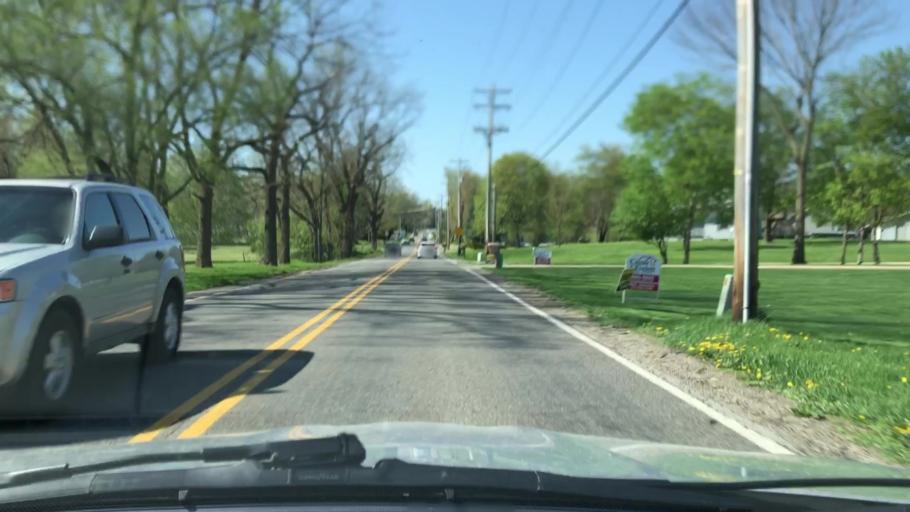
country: US
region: Indiana
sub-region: Saint Joseph County
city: Georgetown
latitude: 41.7495
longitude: -86.3000
